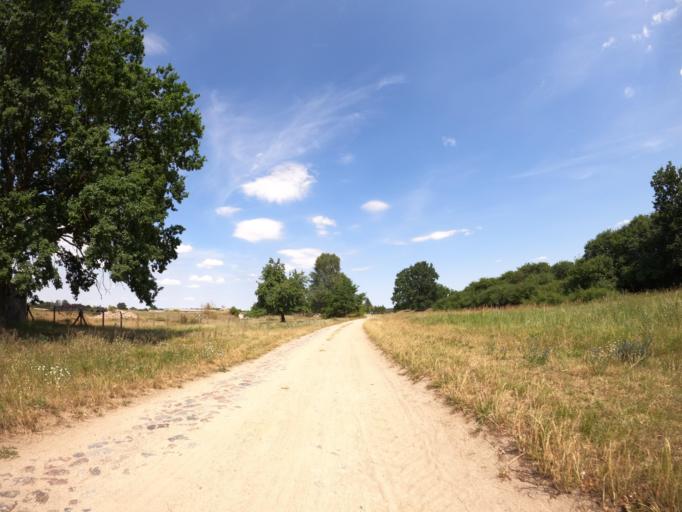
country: DE
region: Brandenburg
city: Mittenwalde
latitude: 53.2955
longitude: 13.5639
